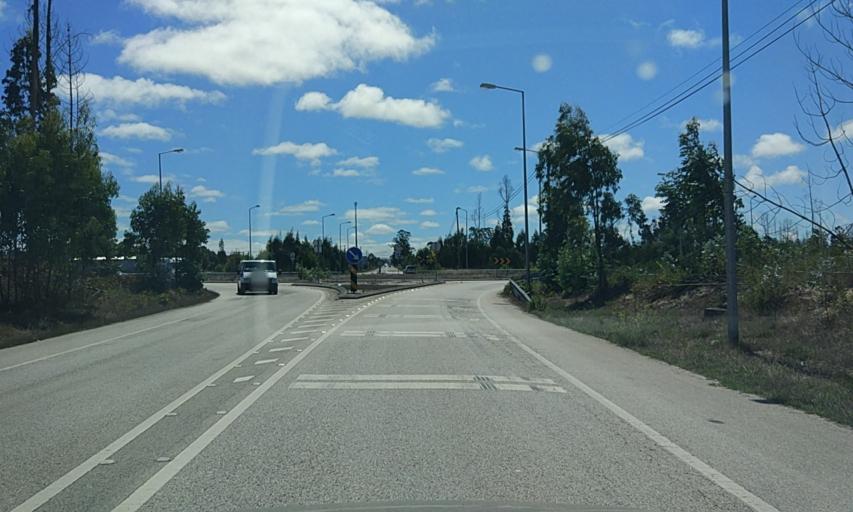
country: PT
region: Coimbra
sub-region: Mira
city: Mira
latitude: 40.3390
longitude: -8.7482
